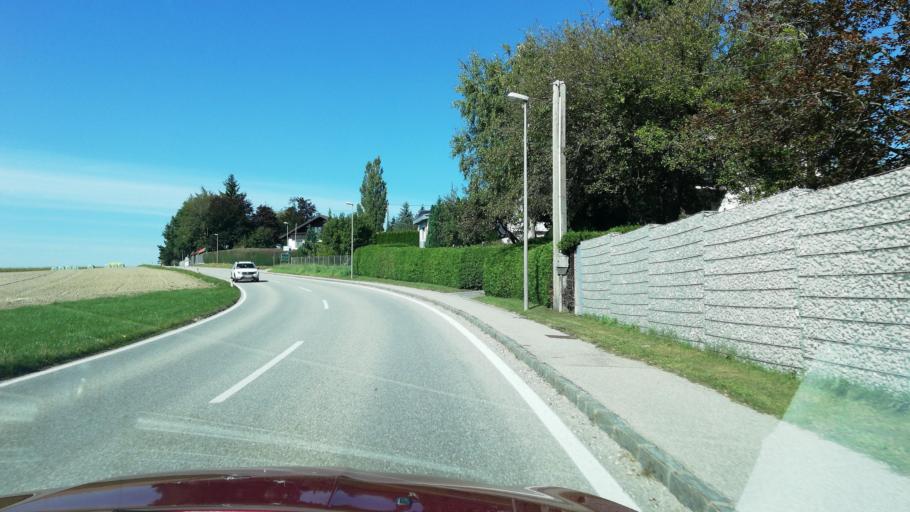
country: AT
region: Upper Austria
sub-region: Politischer Bezirk Vocklabruck
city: Zell am Pettenfirst
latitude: 48.1488
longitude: 13.5684
